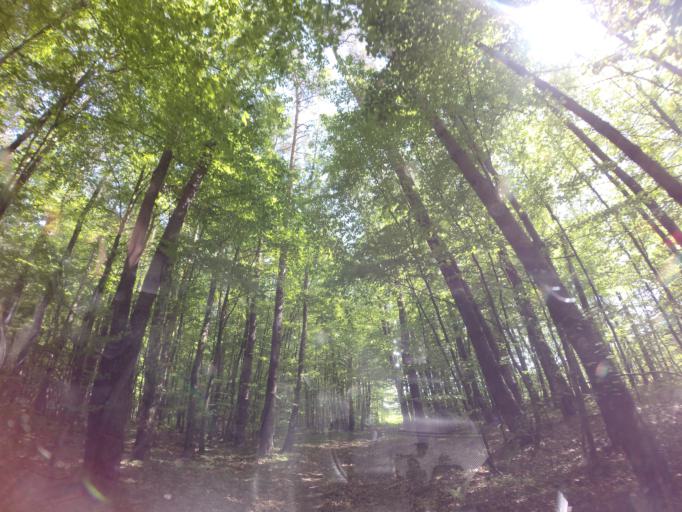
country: PL
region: West Pomeranian Voivodeship
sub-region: Powiat choszczenski
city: Pelczyce
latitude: 52.9474
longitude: 15.3373
